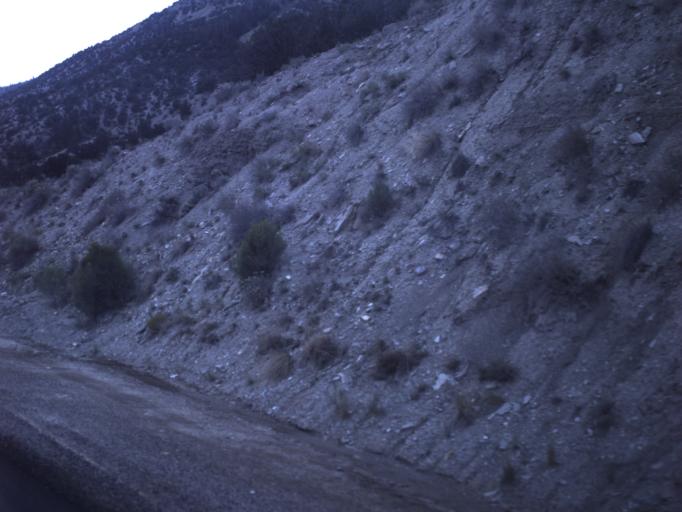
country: US
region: Utah
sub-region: Duchesne County
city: Duchesne
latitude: 39.9550
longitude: -110.6504
